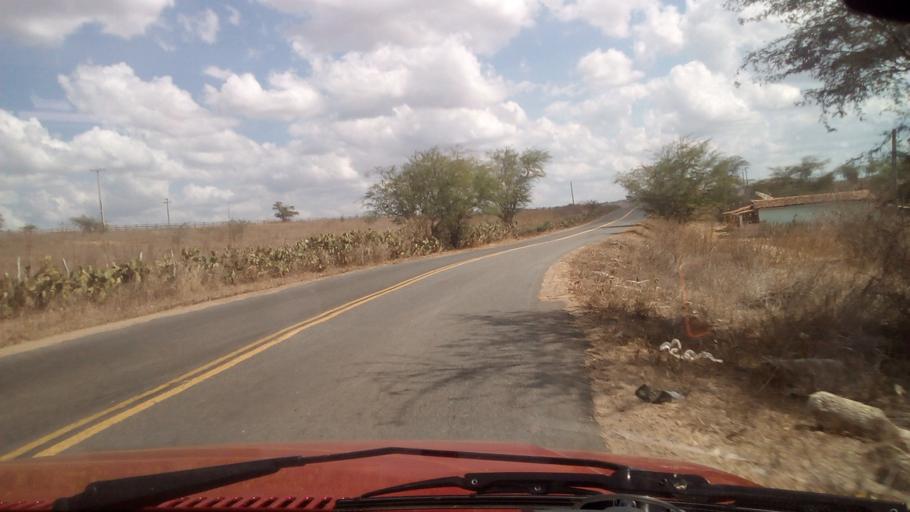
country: BR
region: Paraiba
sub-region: Bananeiras
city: Bananeiras
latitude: -6.7115
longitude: -35.7220
